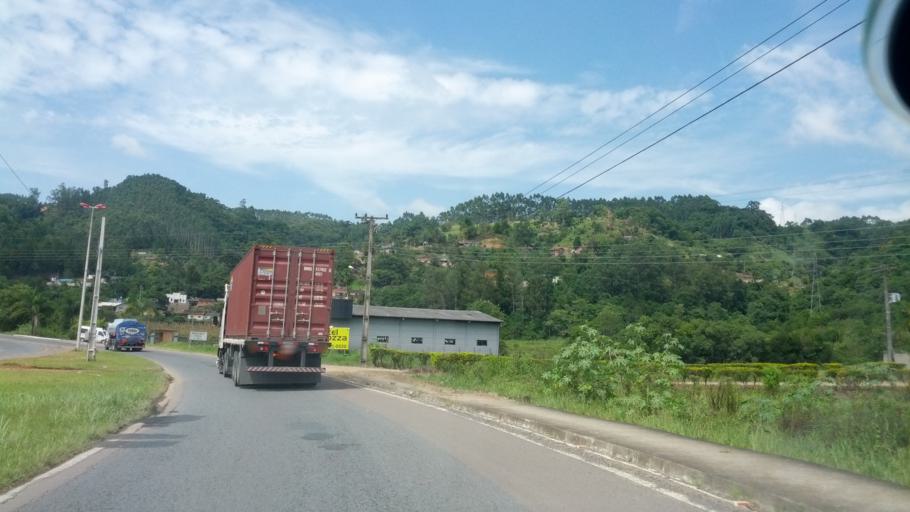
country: BR
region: Santa Catarina
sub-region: Ibirama
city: Ibirama
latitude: -27.0828
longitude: -49.5209
